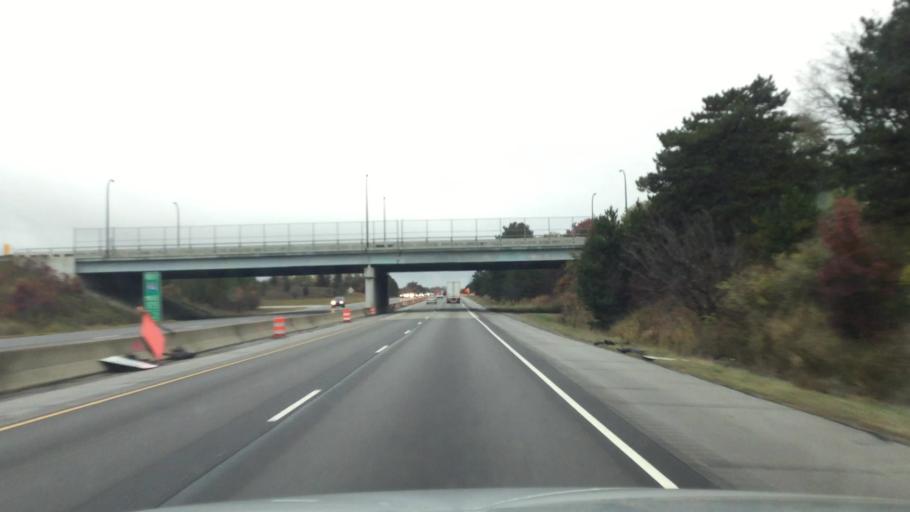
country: US
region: Michigan
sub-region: Washtenaw County
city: Ann Arbor
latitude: 42.2450
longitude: -83.7625
